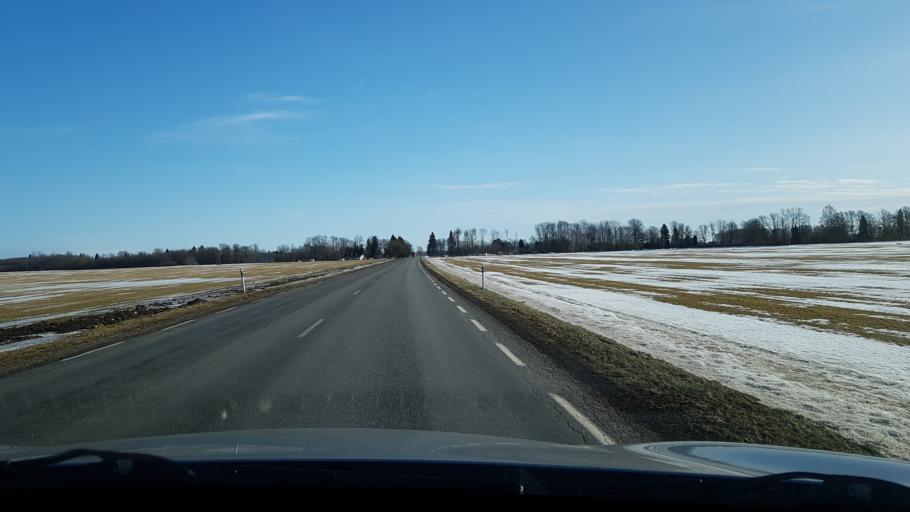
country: EE
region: Viljandimaa
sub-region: Vohma linn
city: Vohma
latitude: 58.6329
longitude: 25.5926
